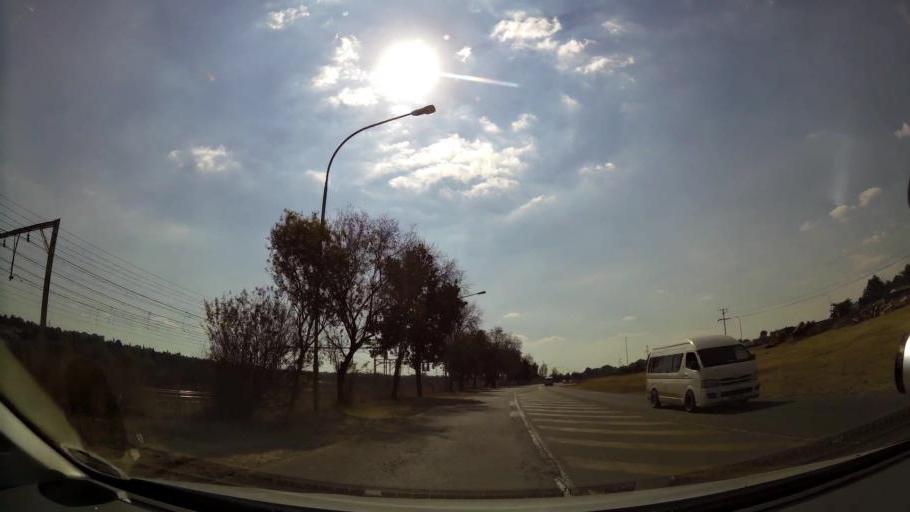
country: ZA
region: Gauteng
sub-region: City of Johannesburg Metropolitan Municipality
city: Modderfontein
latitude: -26.0833
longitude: 28.2234
